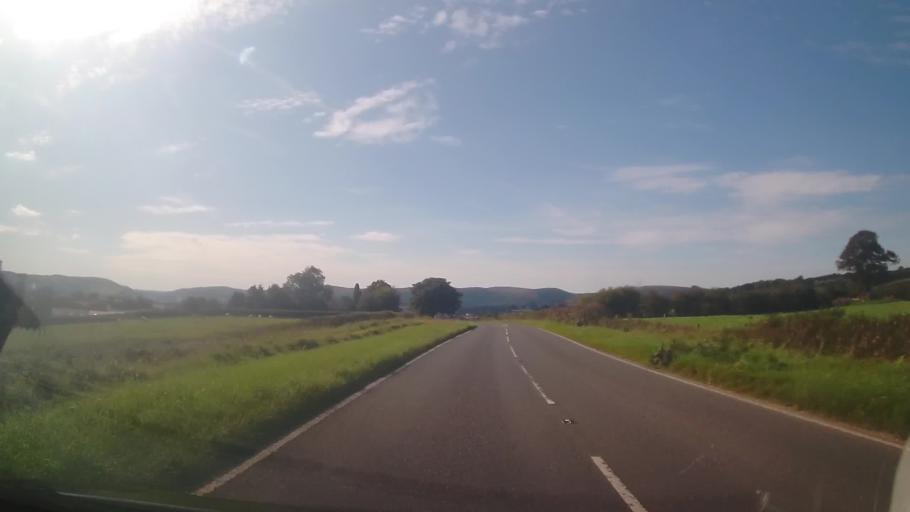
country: GB
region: Wales
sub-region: Sir Powys
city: Rhayader
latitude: 52.3037
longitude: -3.4886
